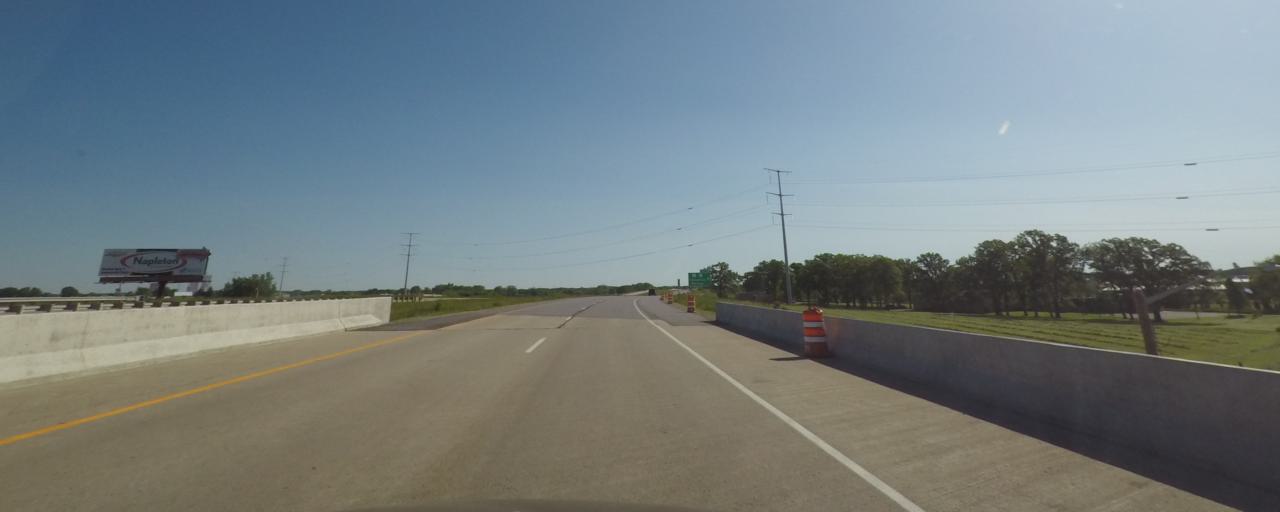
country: US
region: Wisconsin
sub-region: Columbia County
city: Columbus
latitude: 43.3418
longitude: -89.0414
